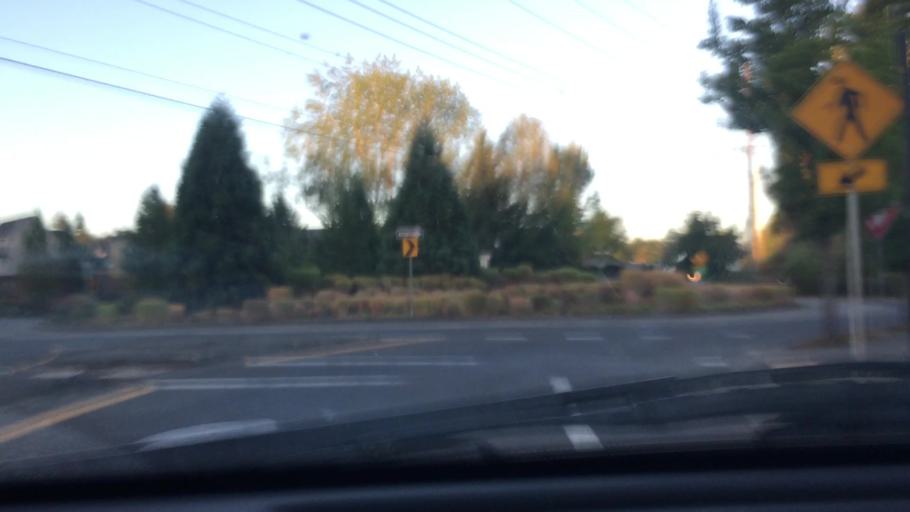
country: US
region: Oregon
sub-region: Washington County
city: Sherwood
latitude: 45.3608
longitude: -122.8247
